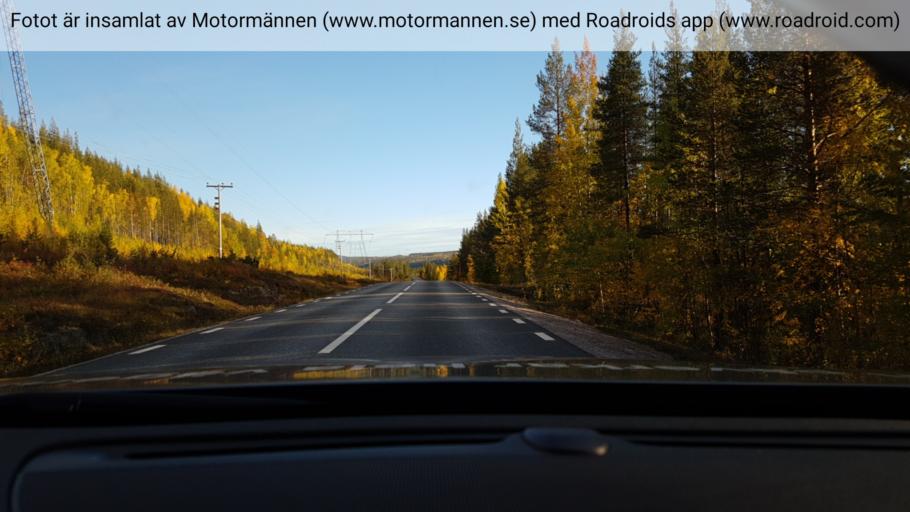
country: SE
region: Norrbotten
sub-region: Jokkmokks Kommun
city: Jokkmokk
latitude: 66.8448
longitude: 19.8369
